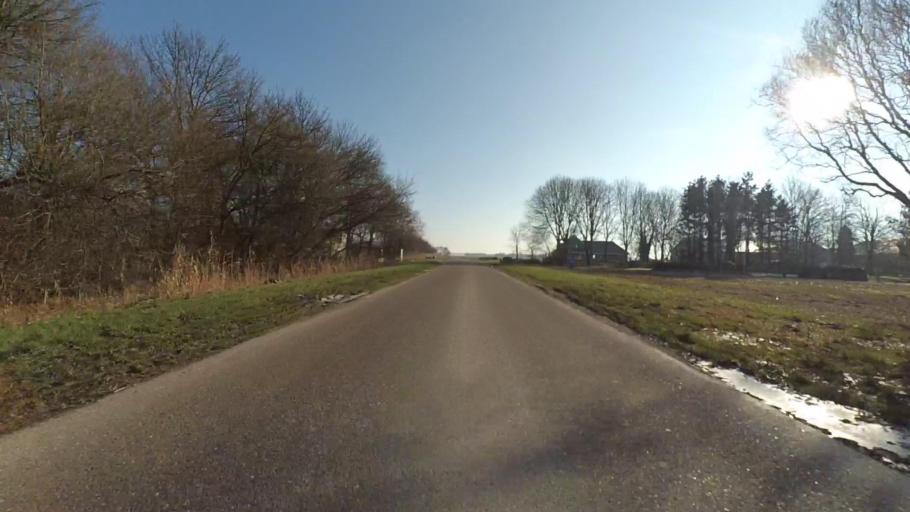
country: NL
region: Utrecht
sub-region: Gemeente Bunschoten
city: Spakenburg
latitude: 52.3044
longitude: 5.3774
